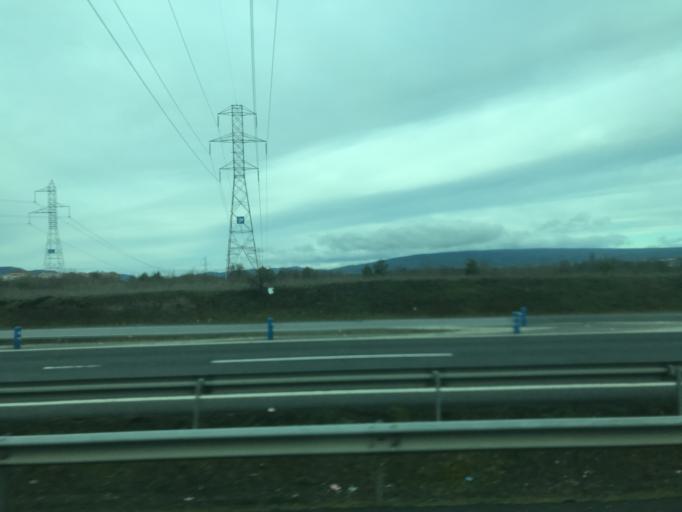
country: ES
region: Basque Country
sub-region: Provincia de Alava
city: Gasteiz / Vitoria
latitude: 42.8744
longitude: -2.6920
